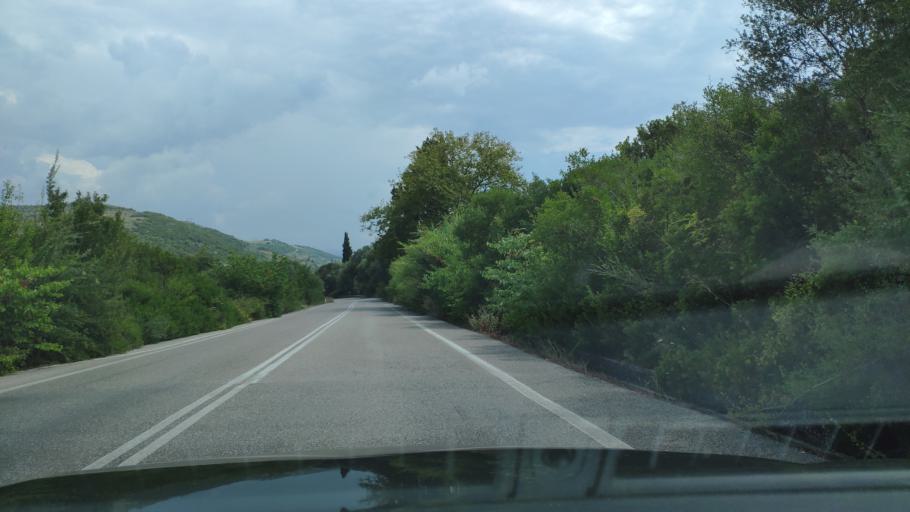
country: GR
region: West Greece
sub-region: Nomos Aitolias kai Akarnanias
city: Krikellos
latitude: 38.9919
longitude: 21.1561
